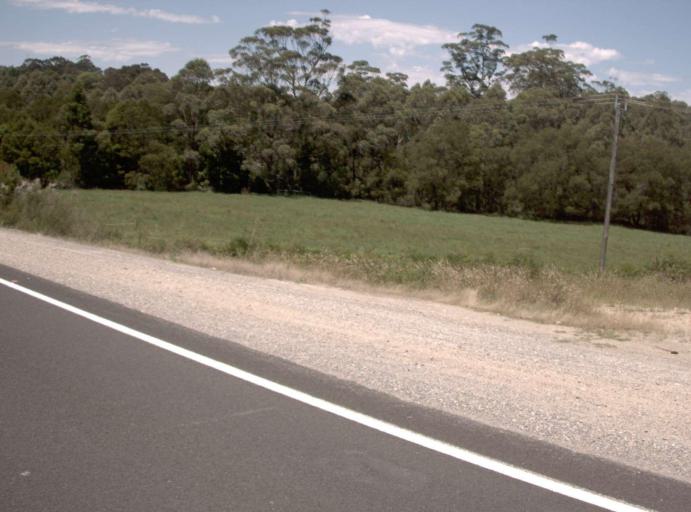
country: AU
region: Victoria
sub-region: East Gippsland
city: Lakes Entrance
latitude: -37.7023
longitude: 148.7148
